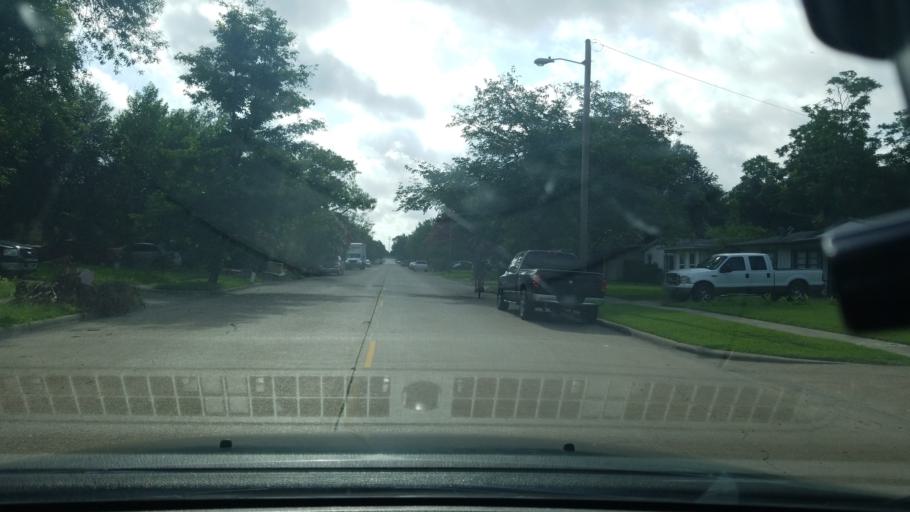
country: US
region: Texas
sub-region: Dallas County
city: Mesquite
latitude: 32.8142
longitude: -96.6726
